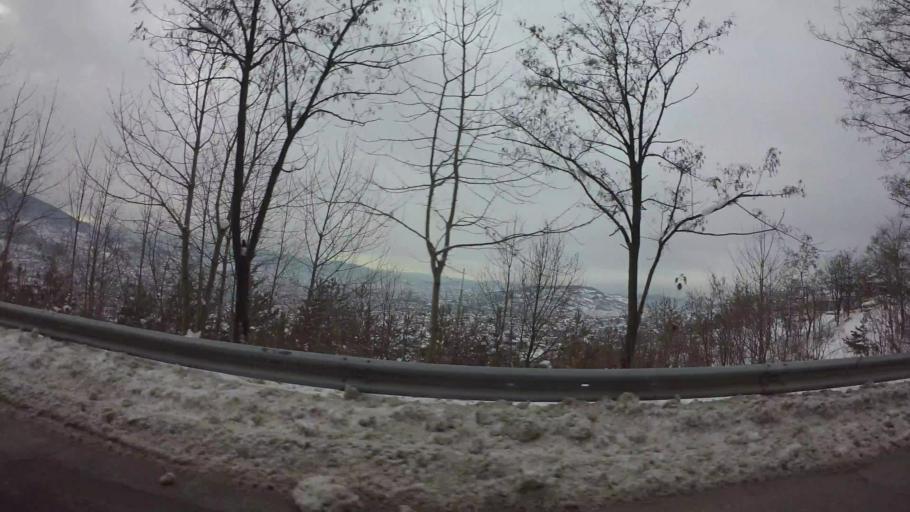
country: BA
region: Federation of Bosnia and Herzegovina
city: Kobilja Glava
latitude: 43.8659
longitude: 18.4428
